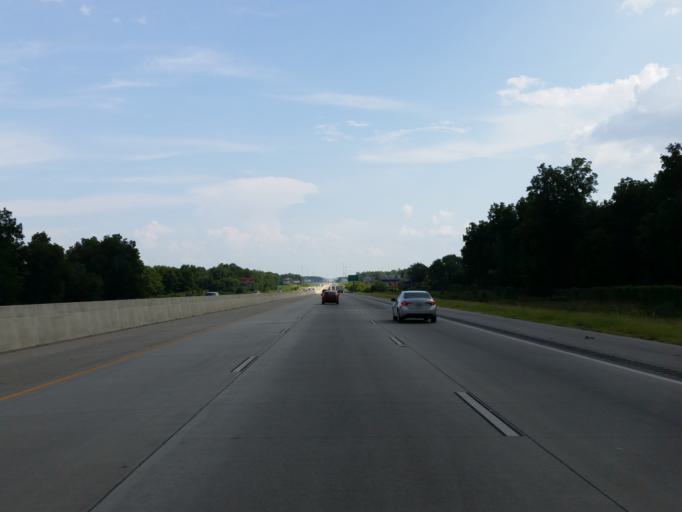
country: US
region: Georgia
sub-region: Crisp County
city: Cordele
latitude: 32.0216
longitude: -83.7614
